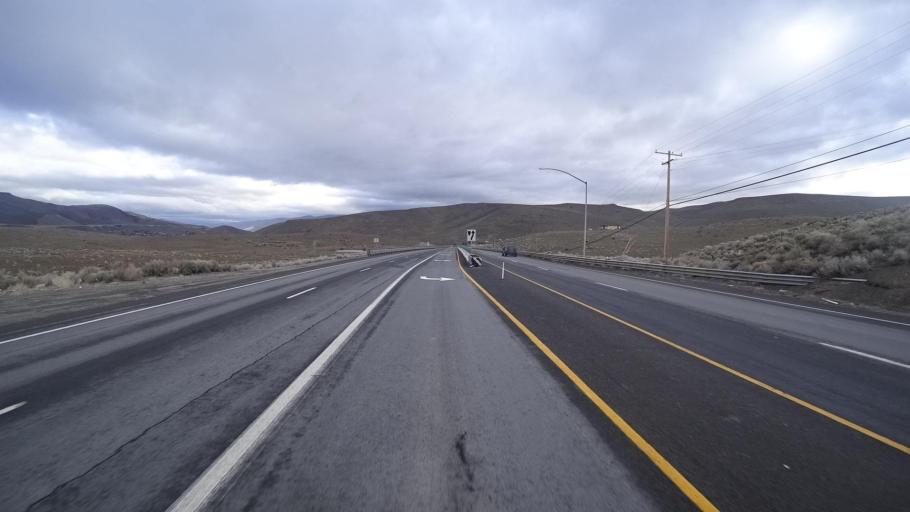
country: US
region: Nevada
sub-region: Storey County
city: Virginia City
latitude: 39.3324
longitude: -119.7899
